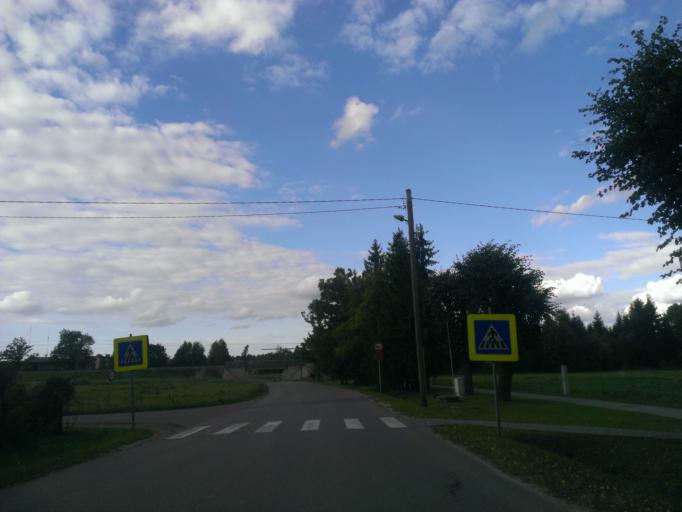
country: LV
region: Sigulda
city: Sigulda
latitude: 57.1542
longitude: 24.8753
